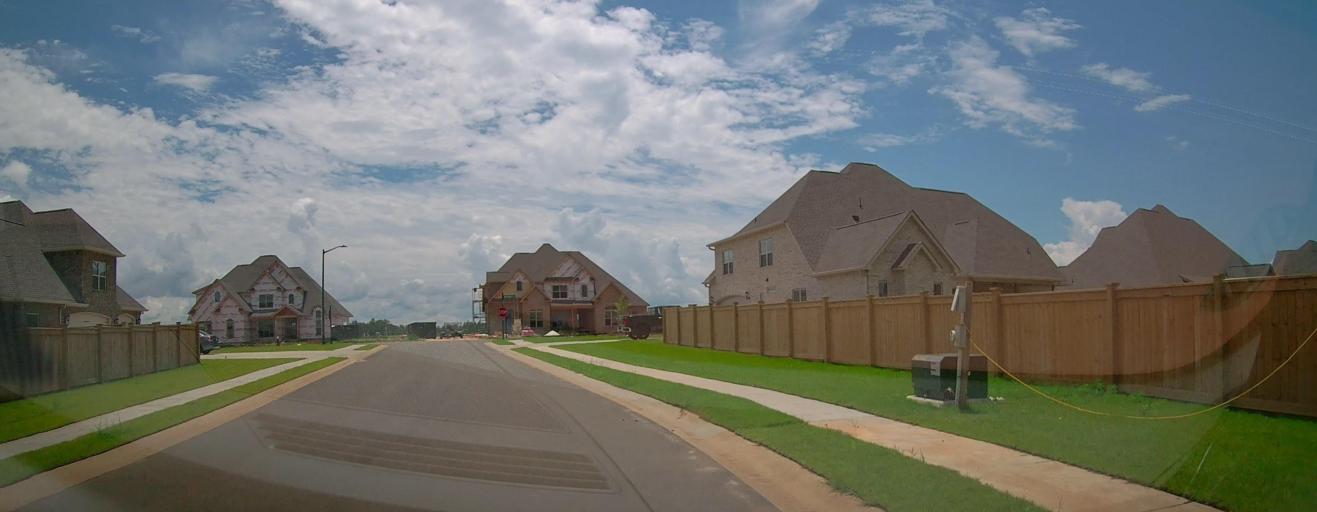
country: US
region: Georgia
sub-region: Houston County
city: Robins Air Force Base
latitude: 32.5151
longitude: -83.6262
